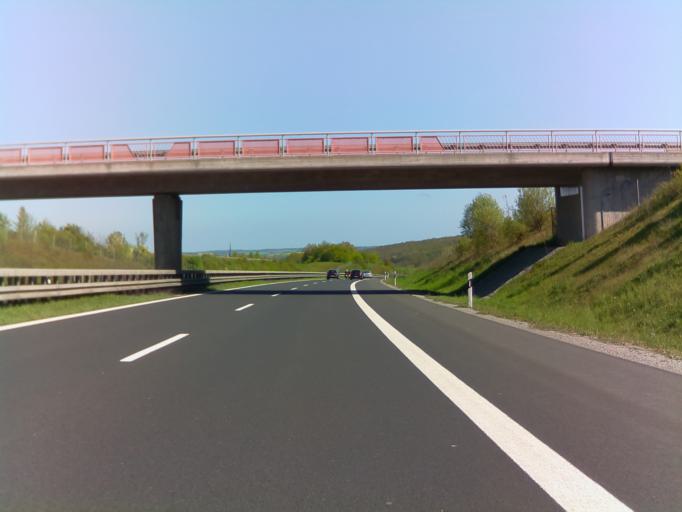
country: DE
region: Bavaria
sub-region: Regierungsbezirk Unterfranken
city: Euerbach
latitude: 50.0714
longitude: 10.1467
